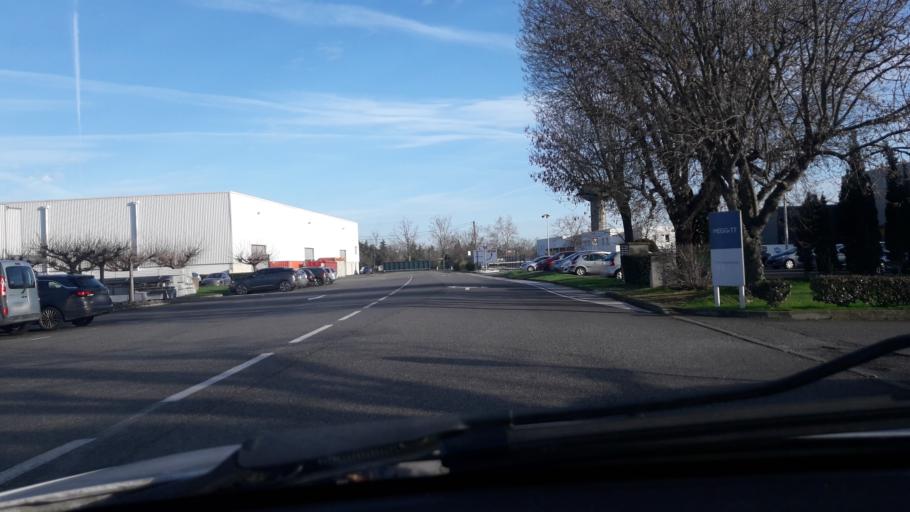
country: FR
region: Midi-Pyrenees
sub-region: Departement de la Haute-Garonne
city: Portet-sur-Garonne
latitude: 43.5564
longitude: 1.4169
